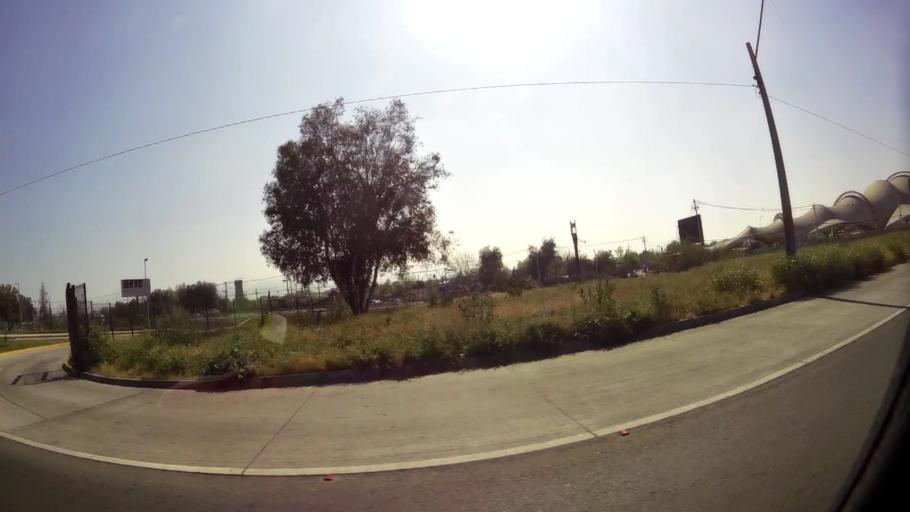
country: CL
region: Santiago Metropolitan
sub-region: Provincia de Santiago
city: Lo Prado
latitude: -33.4911
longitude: -70.7531
